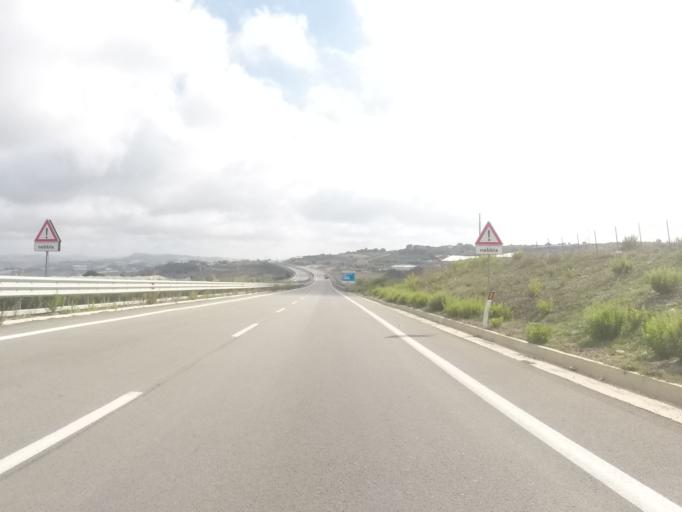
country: IT
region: Sicily
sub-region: Agrigento
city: Canicatti
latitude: 37.3794
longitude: 13.8006
